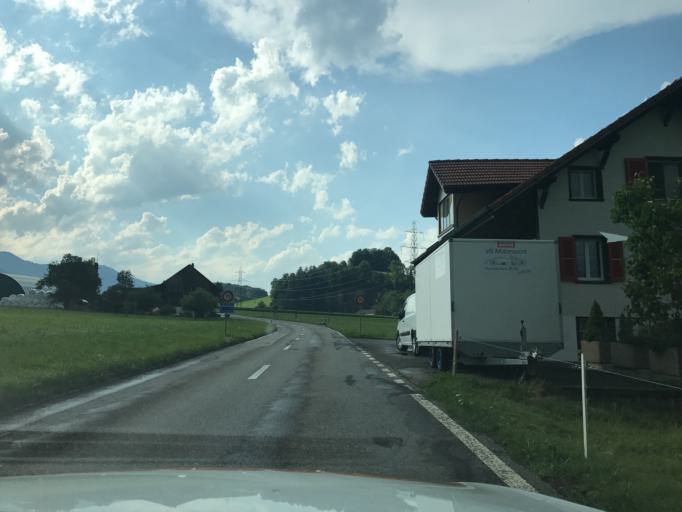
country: CH
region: Bern
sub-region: Thun District
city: Thierachern
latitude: 46.7117
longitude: 7.5722
